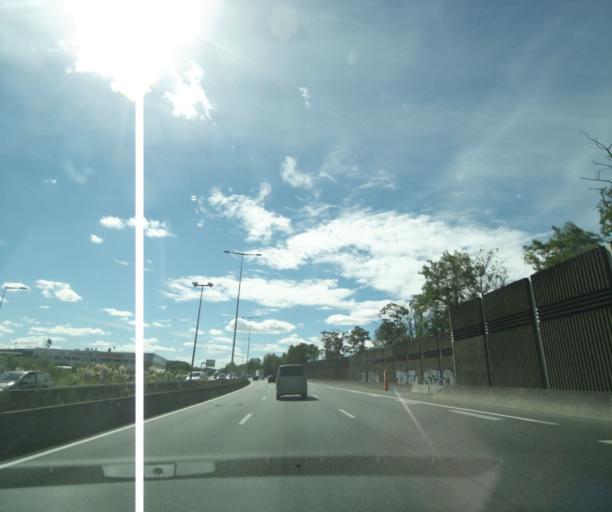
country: FR
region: Aquitaine
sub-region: Departement de la Gironde
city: Ambares-et-Lagrave
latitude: 44.9082
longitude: -0.4907
